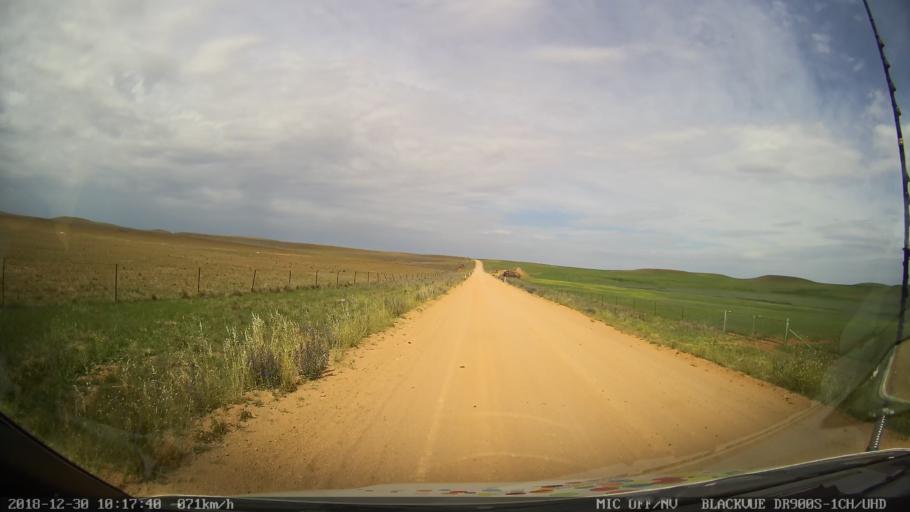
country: AU
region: New South Wales
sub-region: Snowy River
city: Berridale
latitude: -36.5493
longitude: 149.0182
